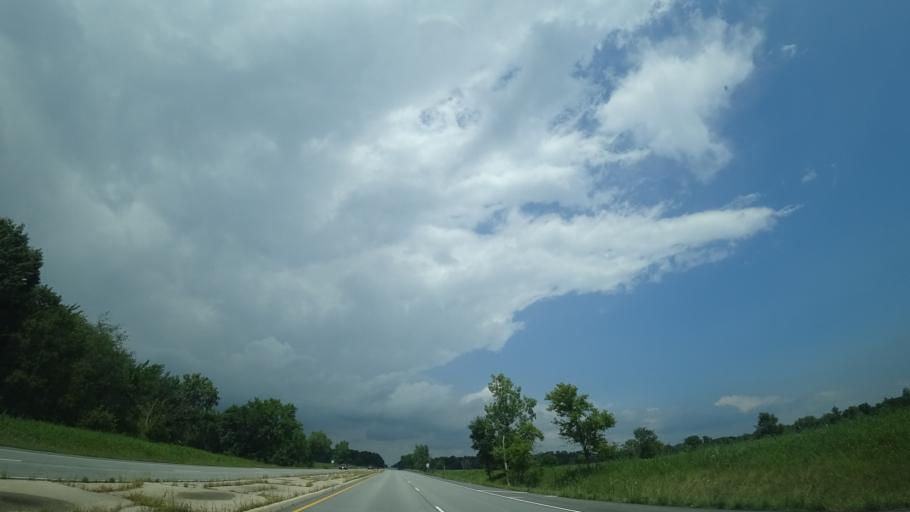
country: US
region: Illinois
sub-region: Cook County
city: Country Club Hills
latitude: 41.5344
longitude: -87.7326
